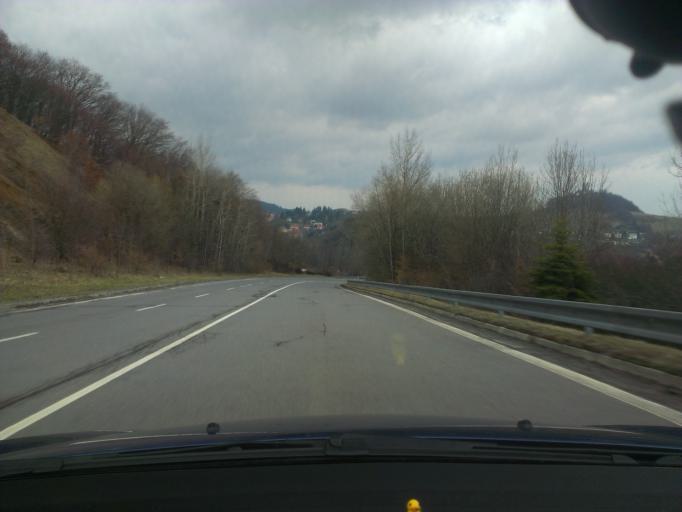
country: SK
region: Banskobystricky
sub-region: Okres Banska Bystrica
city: Banska Stiavnica
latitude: 48.4508
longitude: 18.9007
